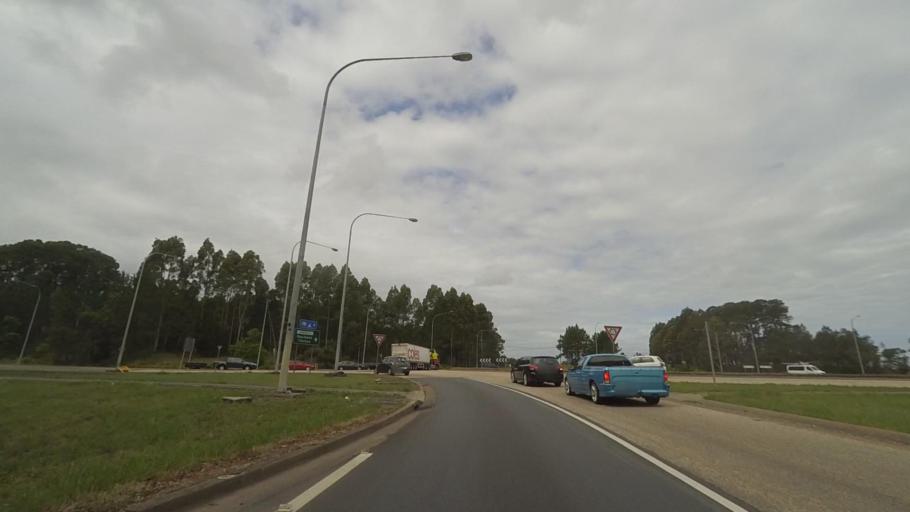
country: AU
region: New South Wales
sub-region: Port Stephens Shire
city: Raymond Terrace
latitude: -32.7816
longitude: 151.7383
